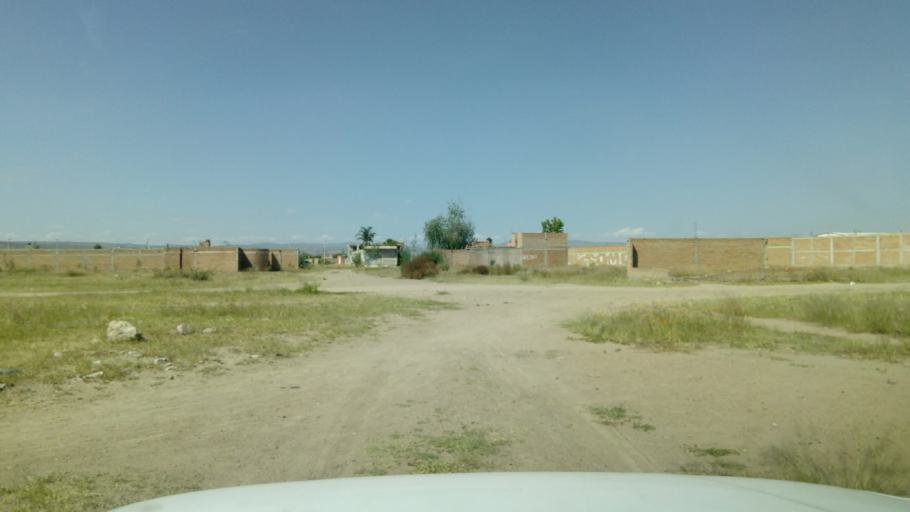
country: MX
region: Durango
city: Victoria de Durango
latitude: 23.9838
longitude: -104.6772
